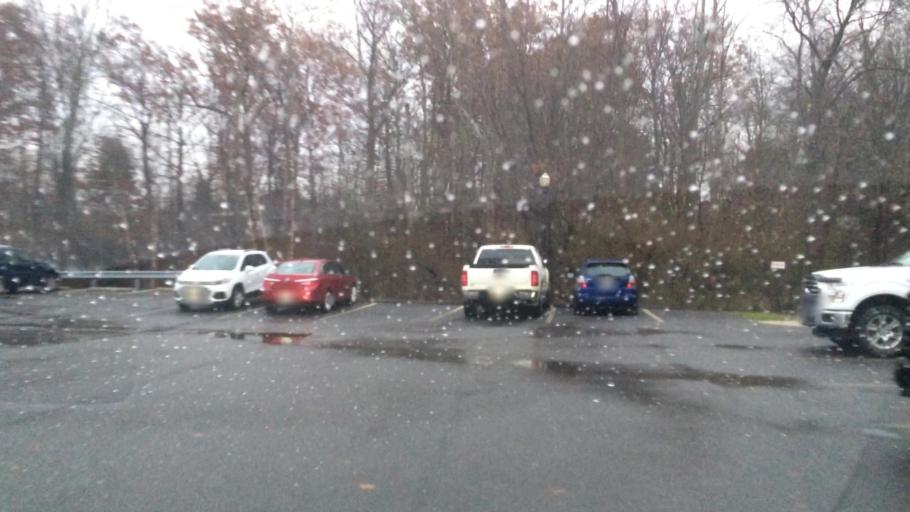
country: US
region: Ohio
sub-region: Cuyahoga County
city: Olmsted Falls
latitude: 41.3658
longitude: -81.9063
